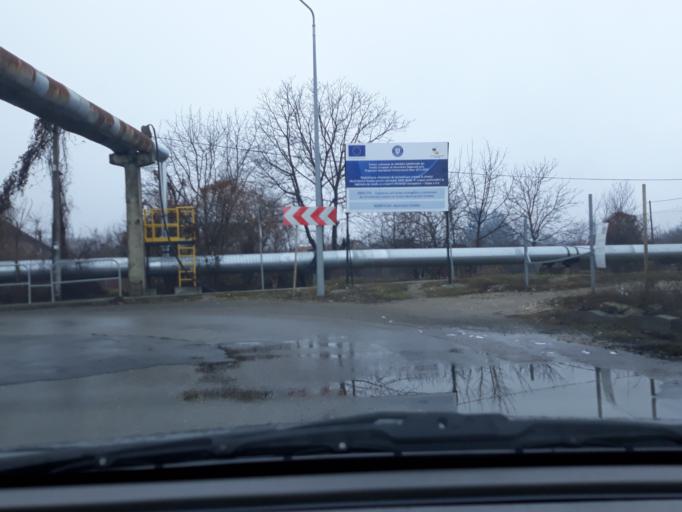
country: RO
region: Bihor
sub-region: Comuna Sanmartin
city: Sanmartin
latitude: 47.0376
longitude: 21.9600
